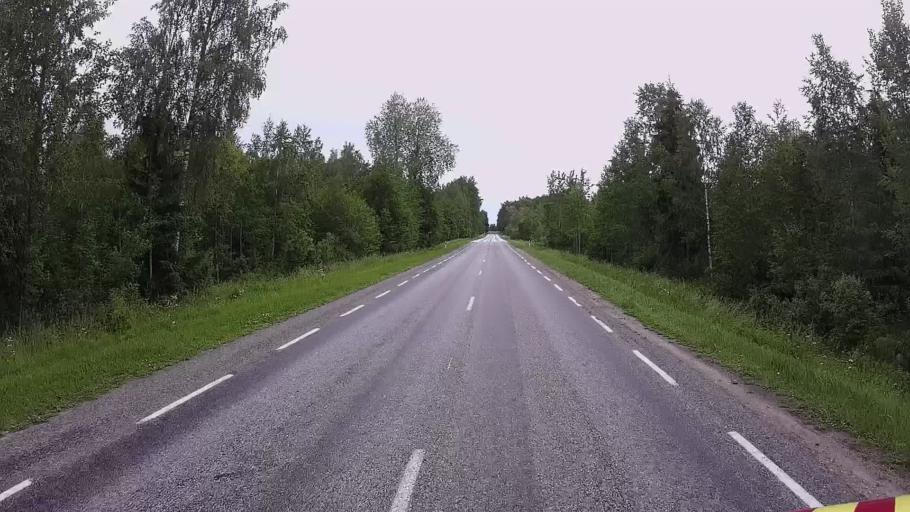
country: EE
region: Viljandimaa
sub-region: Karksi vald
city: Karksi-Nuia
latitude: 58.1898
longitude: 25.6040
